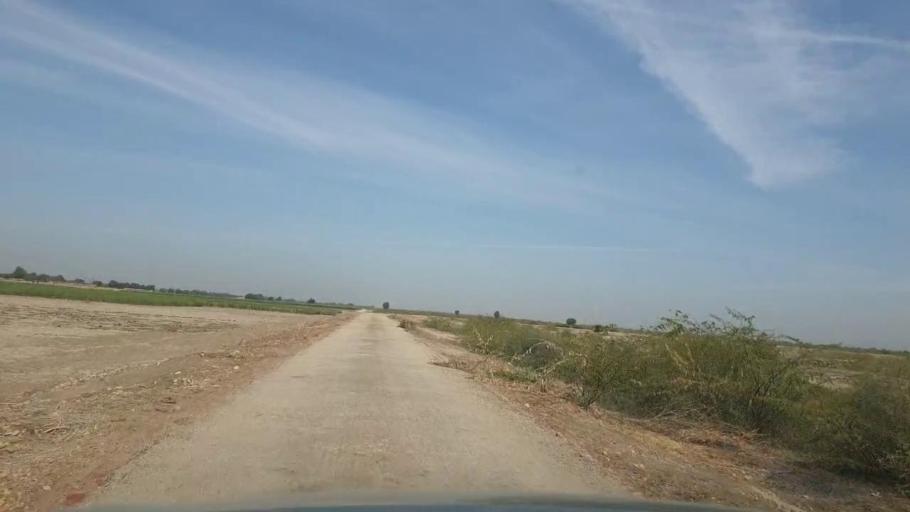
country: PK
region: Sindh
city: Nabisar
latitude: 25.1168
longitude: 69.6131
